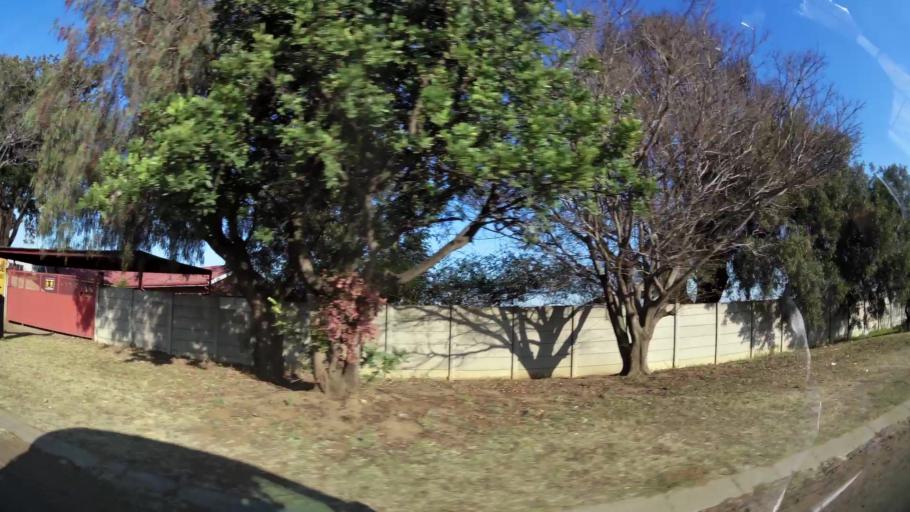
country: ZA
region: Gauteng
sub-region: West Rand District Municipality
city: Randfontein
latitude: -26.2059
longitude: 27.6938
